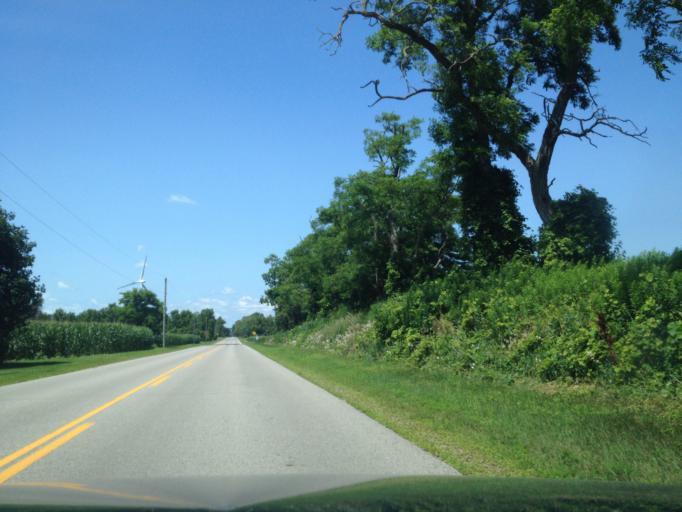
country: CA
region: Ontario
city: Aylmer
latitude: 42.6107
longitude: -80.6879
